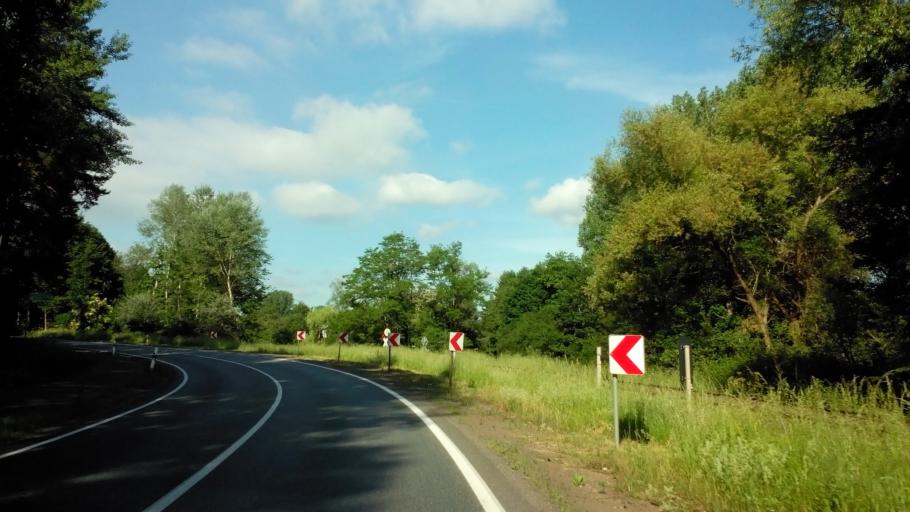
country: DE
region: Saarland
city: Saarwellingen
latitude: 49.3799
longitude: 6.8110
